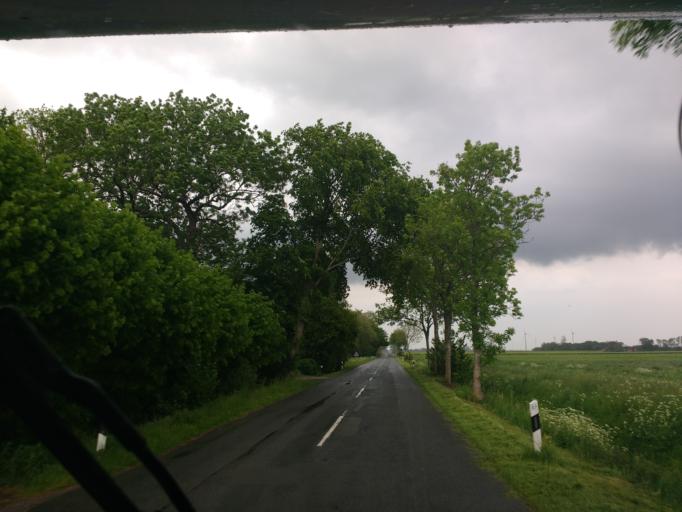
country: DE
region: Lower Saxony
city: Wangerooge
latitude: 53.6934
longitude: 7.8624
